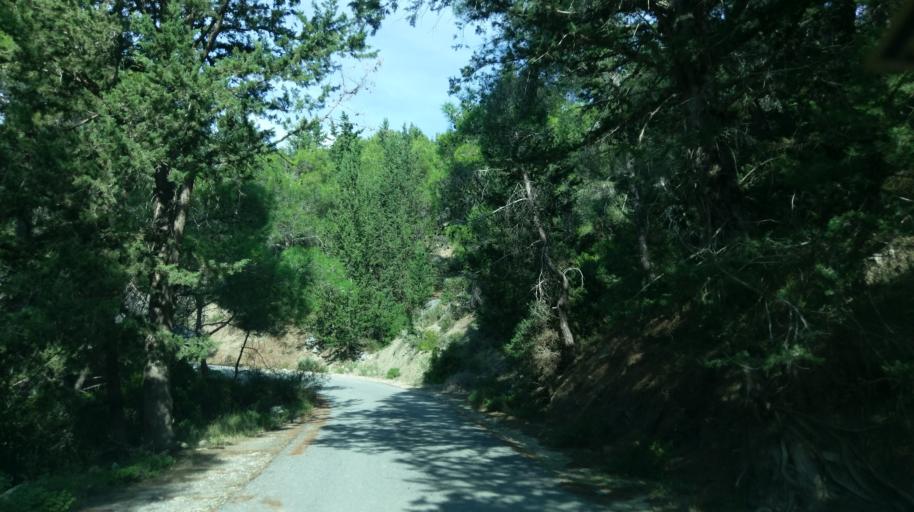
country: CY
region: Keryneia
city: Lapithos
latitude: 35.3290
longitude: 33.1146
